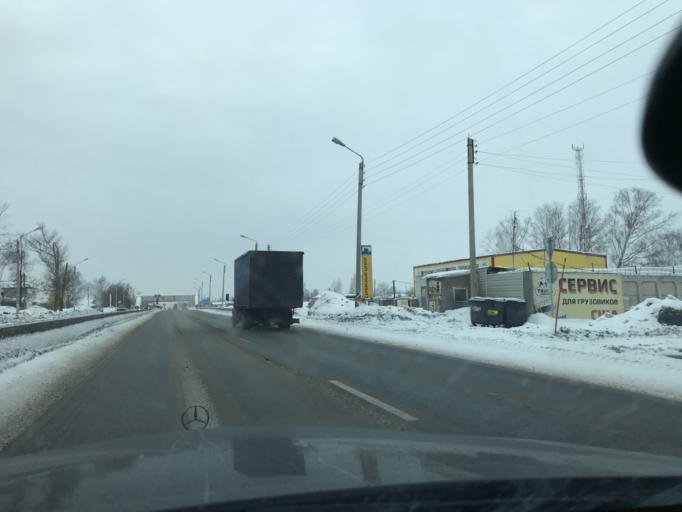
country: RU
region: Nizjnij Novgorod
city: Pyra
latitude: 56.2935
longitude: 43.3597
